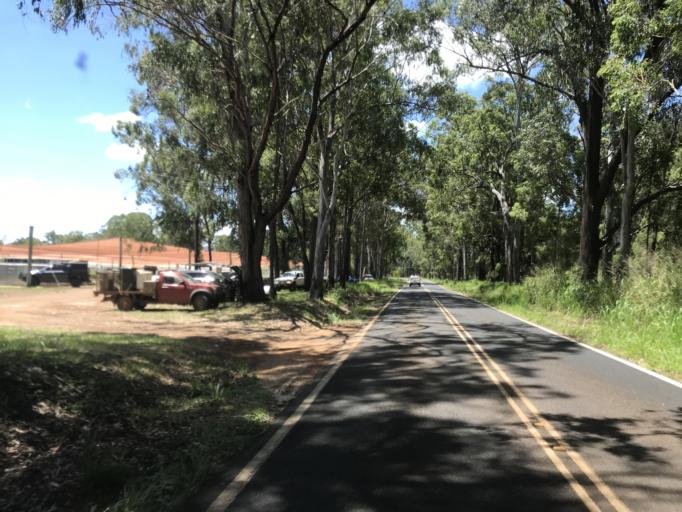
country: AU
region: Queensland
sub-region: Tablelands
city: Atherton
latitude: -17.4247
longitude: 145.3978
